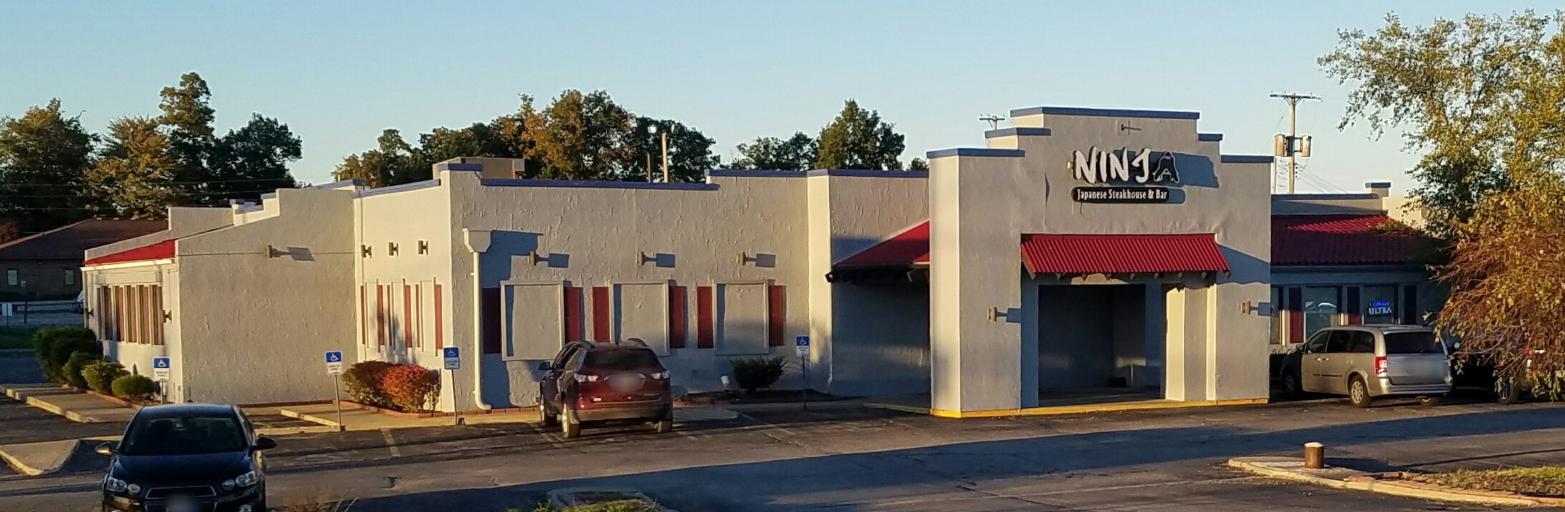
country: US
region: Ohio
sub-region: Richland County
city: Ontario
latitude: 40.7734
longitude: -82.5964
